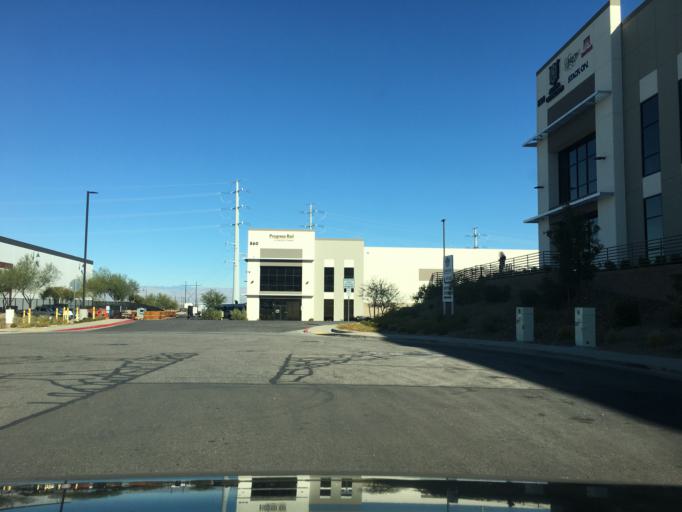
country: US
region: Nevada
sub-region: Clark County
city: Henderson
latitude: 36.0356
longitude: -115.0206
